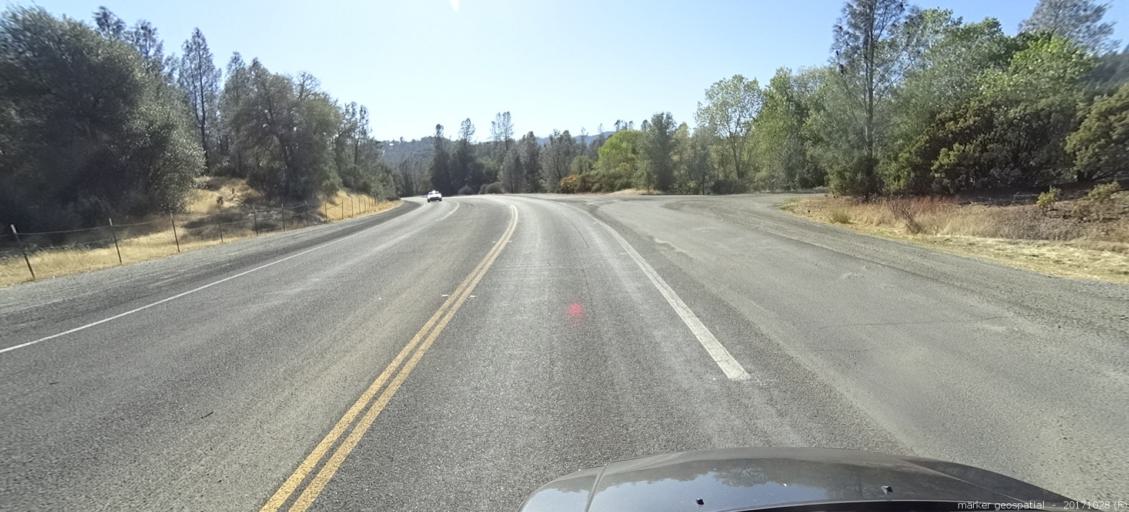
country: US
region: California
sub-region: Shasta County
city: Shasta
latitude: 40.6030
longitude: -122.4643
